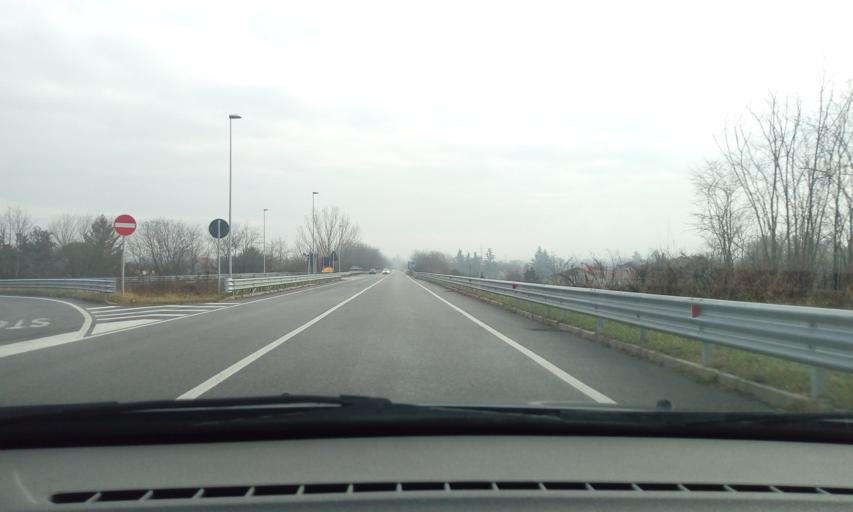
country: IT
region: Friuli Venezia Giulia
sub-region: Provincia di Gorizia
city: Savogna d'Isonzo
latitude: 45.9234
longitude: 13.5671
